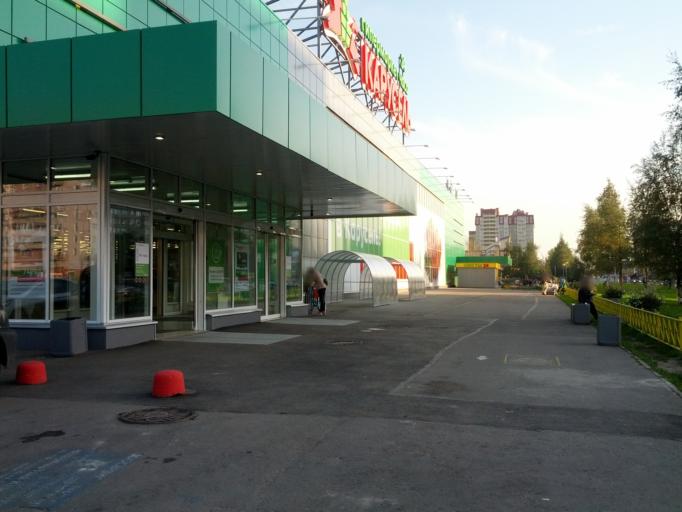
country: RU
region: Leningrad
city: Rybatskoye
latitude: 59.8960
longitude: 30.4926
